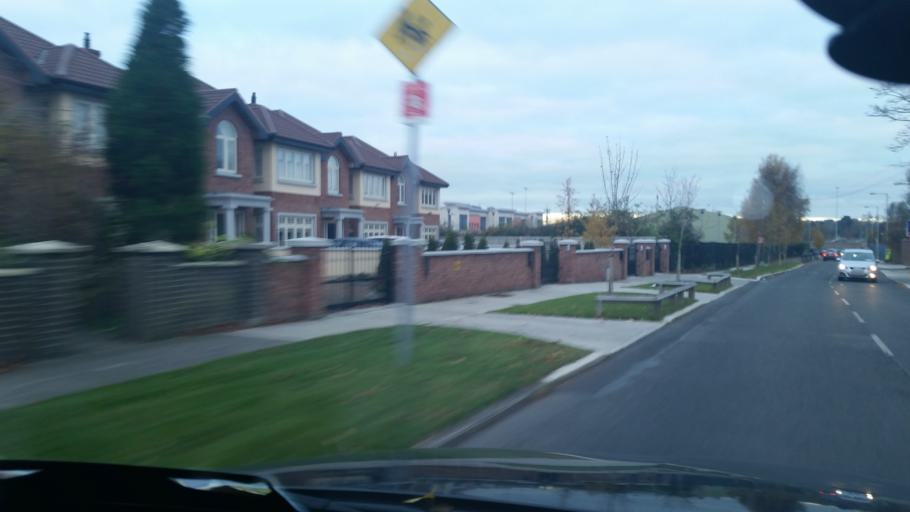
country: IE
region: Leinster
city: Castleknock
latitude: 53.3788
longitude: -6.3616
